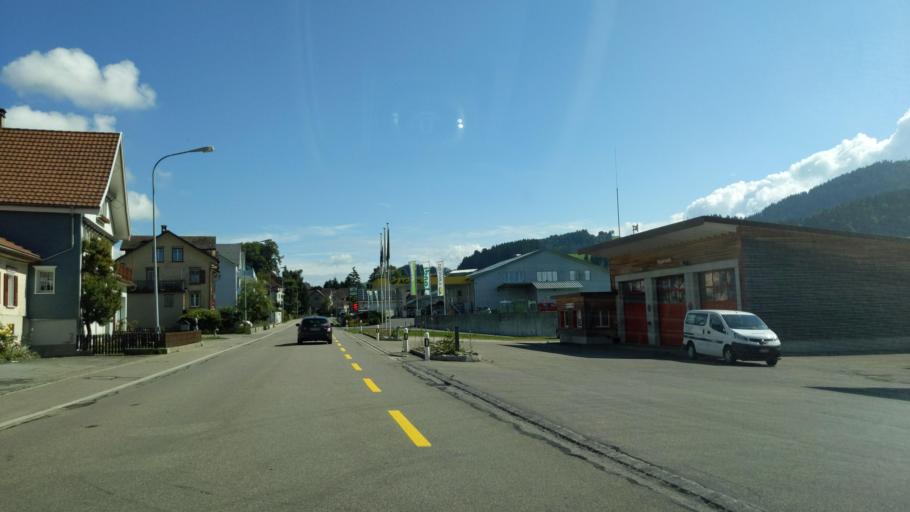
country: CH
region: Appenzell Ausserrhoden
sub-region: Bezirk Hinterland
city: Schwellbrunn
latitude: 47.3277
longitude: 9.2202
